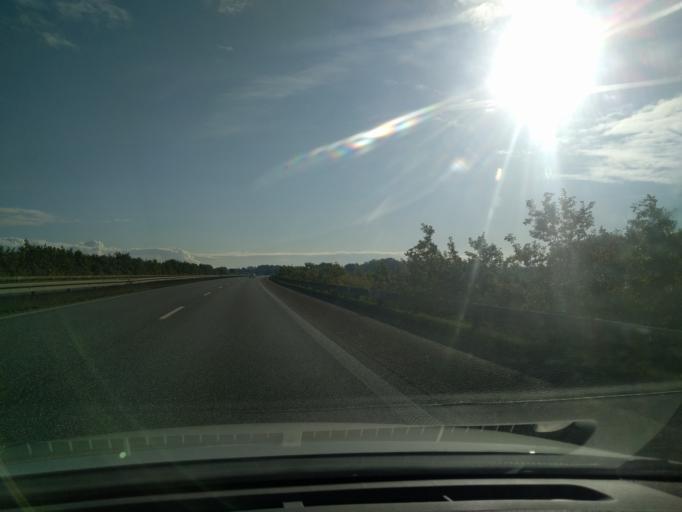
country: DK
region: Zealand
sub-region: Soro Kommune
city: Soro
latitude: 55.4514
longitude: 11.5859
